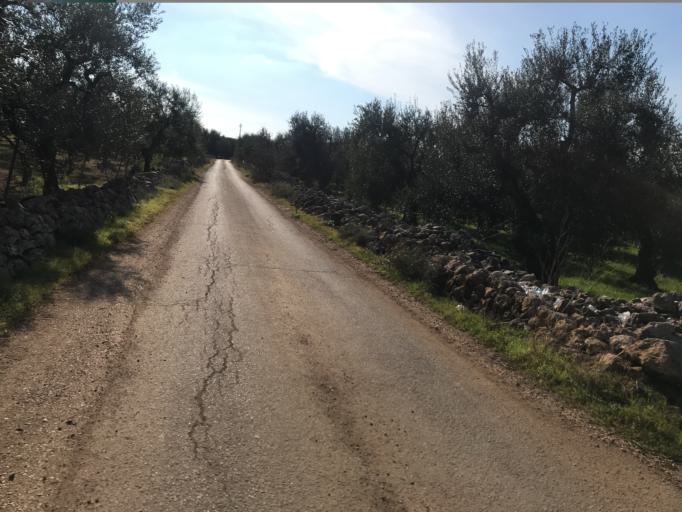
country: IT
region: Apulia
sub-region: Provincia di Bari
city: Corato
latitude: 41.1639
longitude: 16.4313
